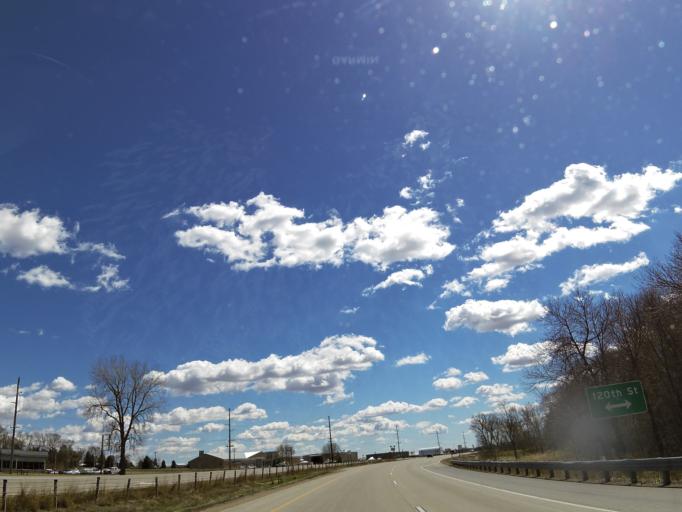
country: US
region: Minnesota
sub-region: Dakota County
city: Hastings
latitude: 44.7775
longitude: -92.8640
